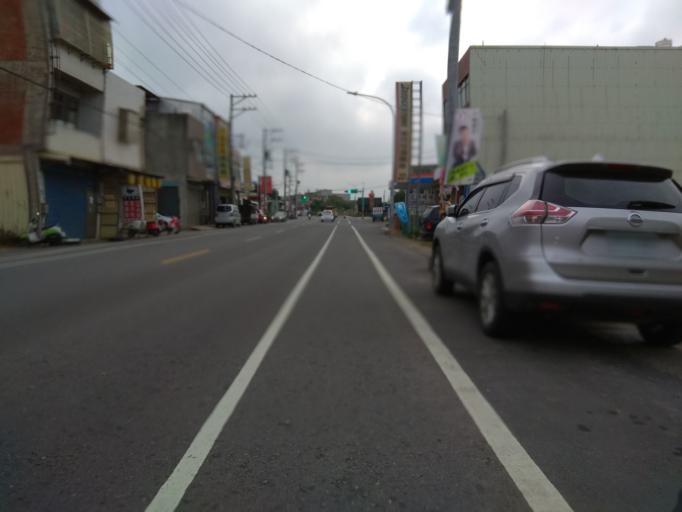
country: TW
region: Taiwan
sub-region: Hsinchu
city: Zhubei
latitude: 24.9714
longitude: 121.1100
